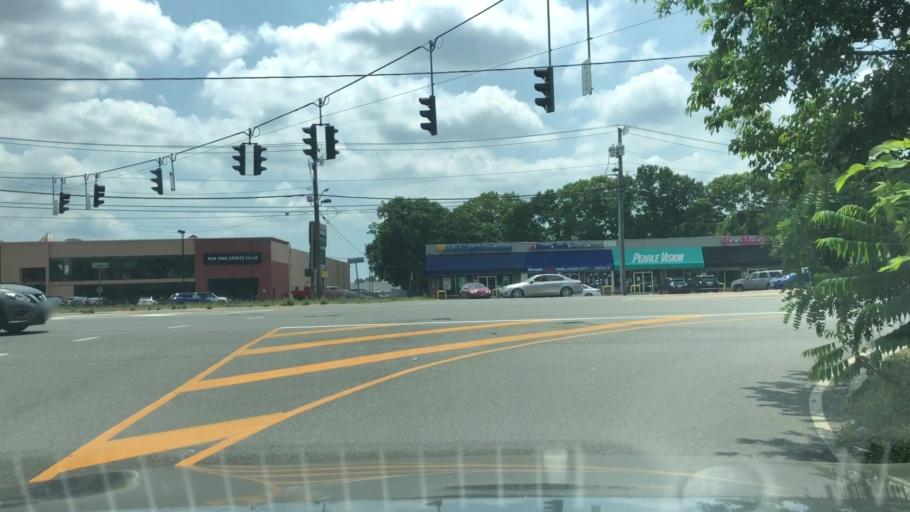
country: US
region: New York
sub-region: Nassau County
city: East Massapequa
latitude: 40.6790
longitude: -73.4376
